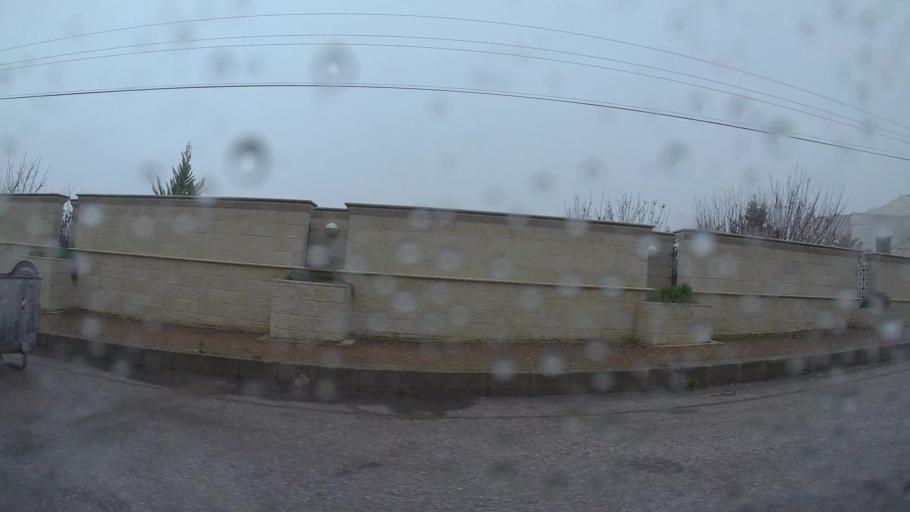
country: JO
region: Amman
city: Wadi as Sir
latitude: 31.9967
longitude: 35.8198
